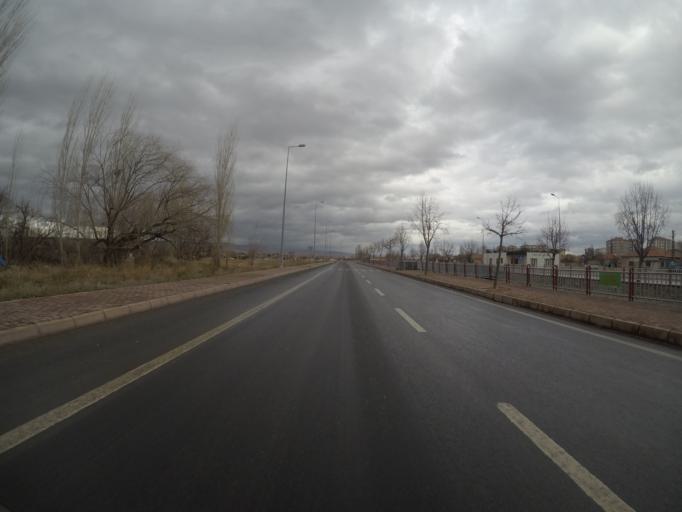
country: TR
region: Kayseri
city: Kayseri
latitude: 38.7531
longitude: 35.4765
